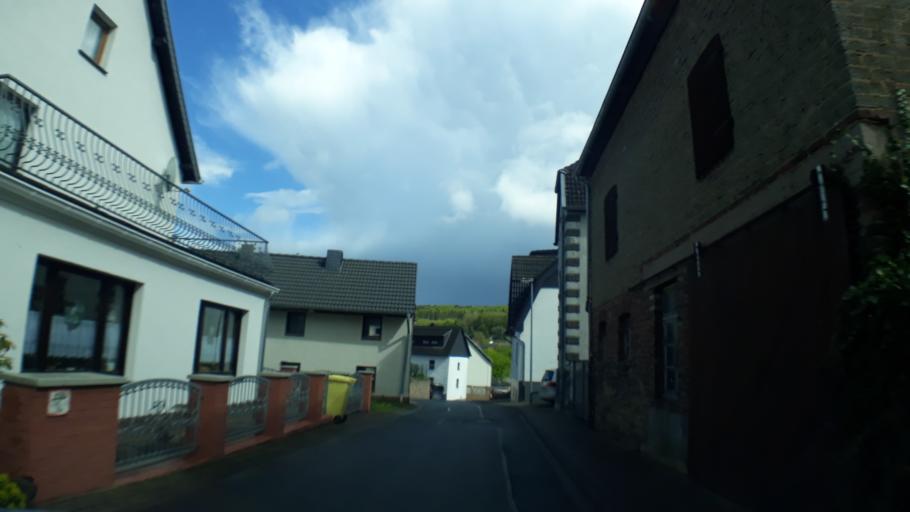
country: DE
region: North Rhine-Westphalia
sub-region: Regierungsbezirk Koln
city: Kall
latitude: 50.5256
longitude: 6.5550
